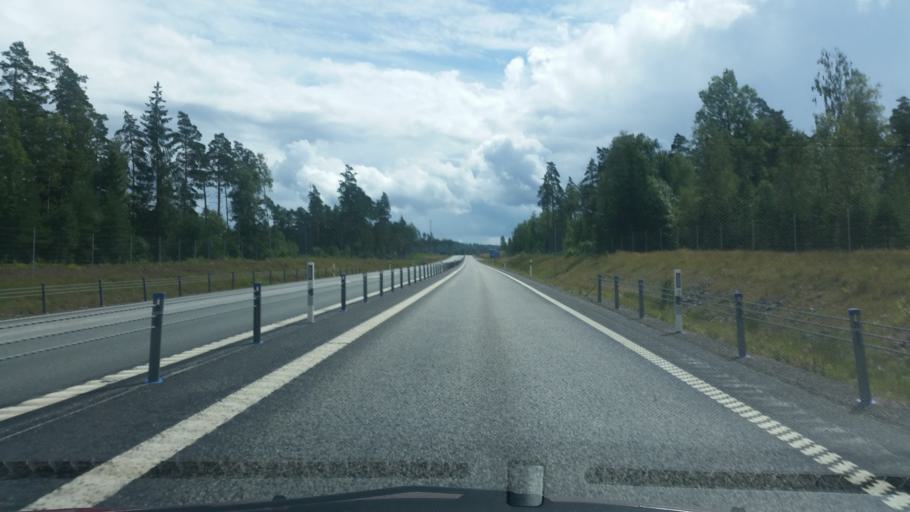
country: SE
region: Joenkoeping
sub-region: Gislaveds Kommun
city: Gislaved
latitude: 57.2896
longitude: 13.5972
